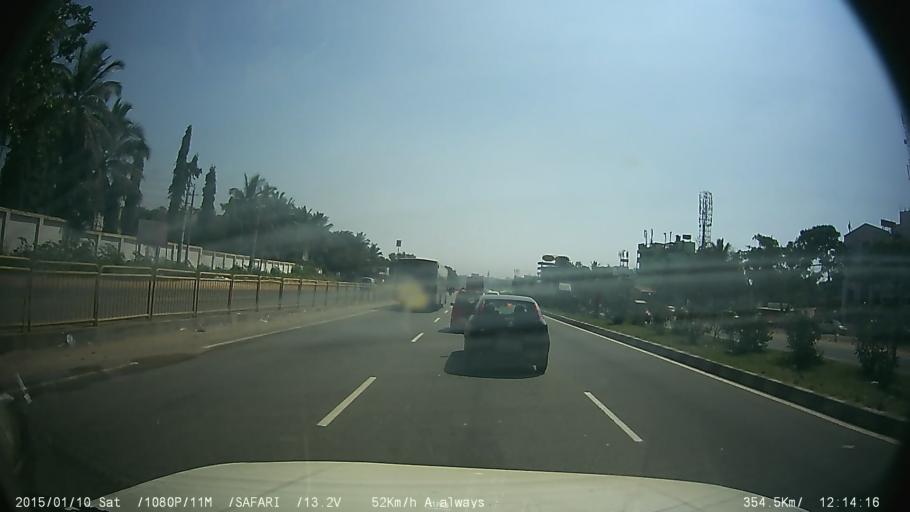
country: IN
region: Karnataka
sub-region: Bangalore Urban
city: Anekal
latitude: 12.8101
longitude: 77.6962
